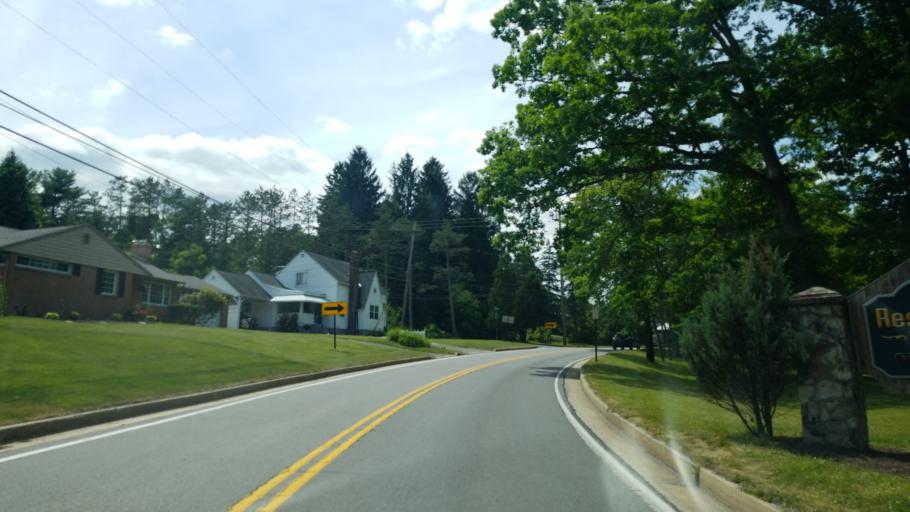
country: US
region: Pennsylvania
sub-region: Blair County
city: Tyrone
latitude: 40.6786
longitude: -78.2526
